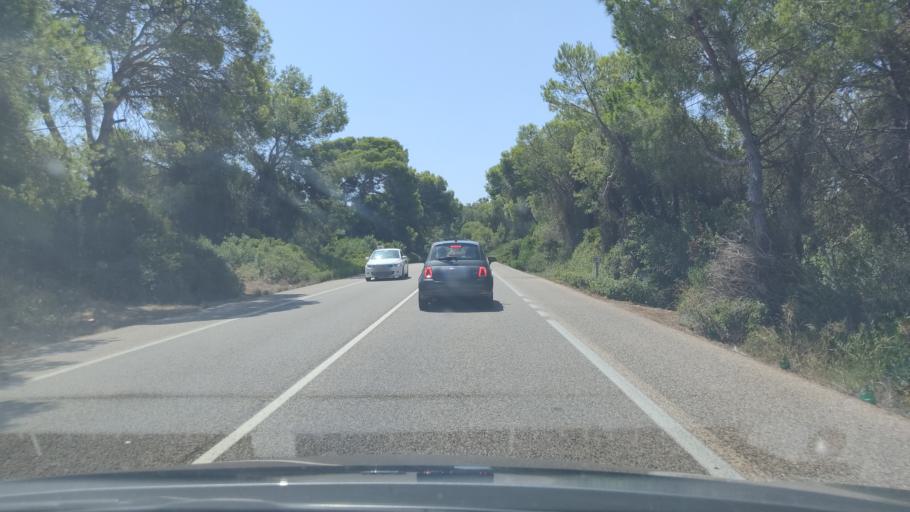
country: ES
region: Valencia
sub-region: Provincia de Valencia
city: Sollana
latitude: 39.3255
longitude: -0.3108
